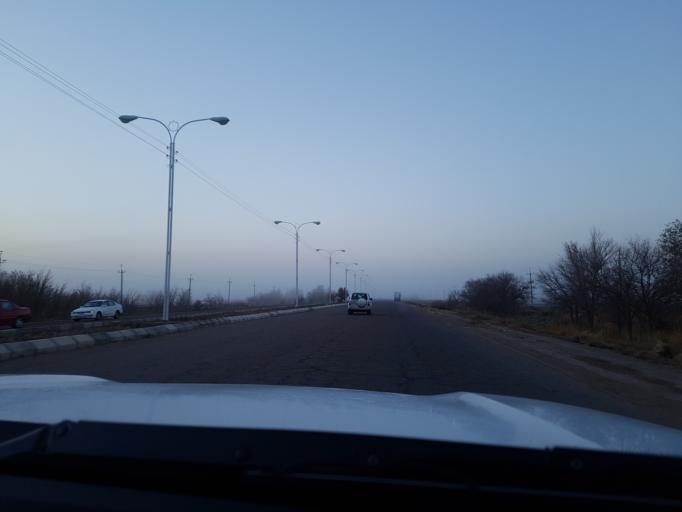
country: TM
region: Dasoguz
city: Koeneuergench
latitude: 41.7403
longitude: 58.6870
